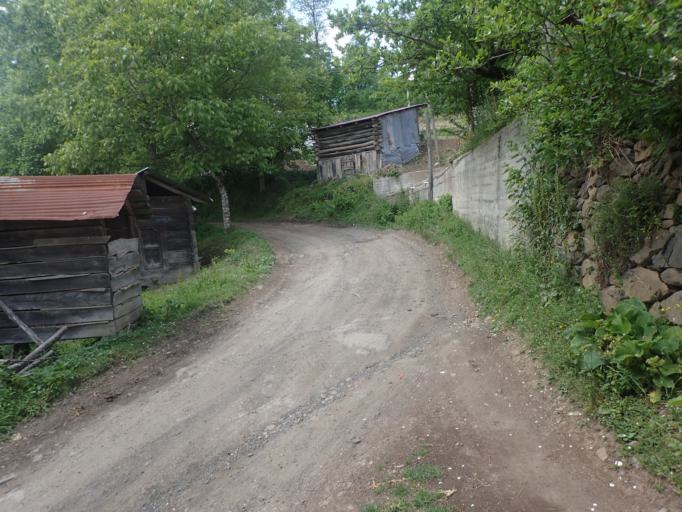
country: TR
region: Samsun
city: Salipazari
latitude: 40.9234
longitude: 36.8549
